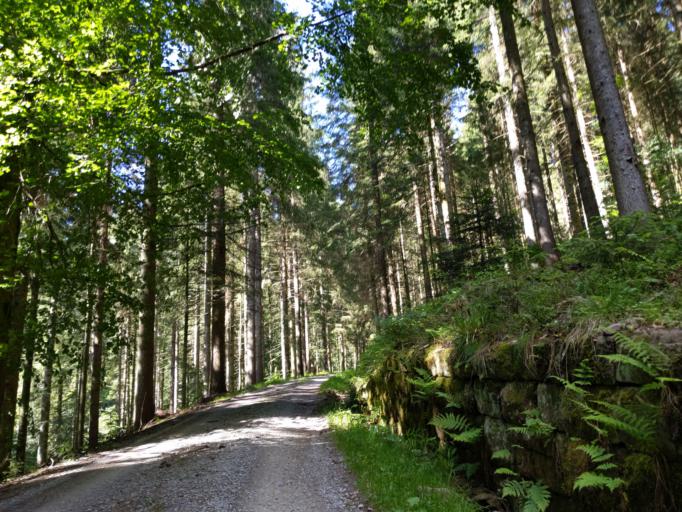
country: DE
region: Baden-Wuerttemberg
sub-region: Karlsruhe Region
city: Bad Rippoldsau-Schapbach
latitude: 48.4170
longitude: 8.3812
